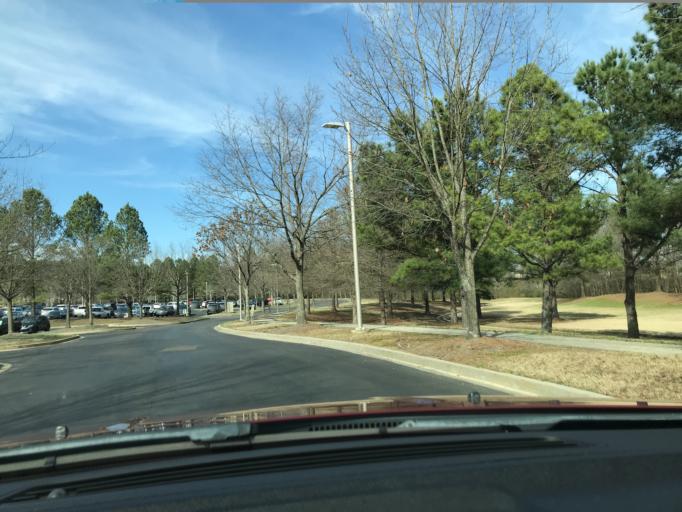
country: US
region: Tennessee
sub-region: Shelby County
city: Collierville
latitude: 35.0327
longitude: -89.7192
